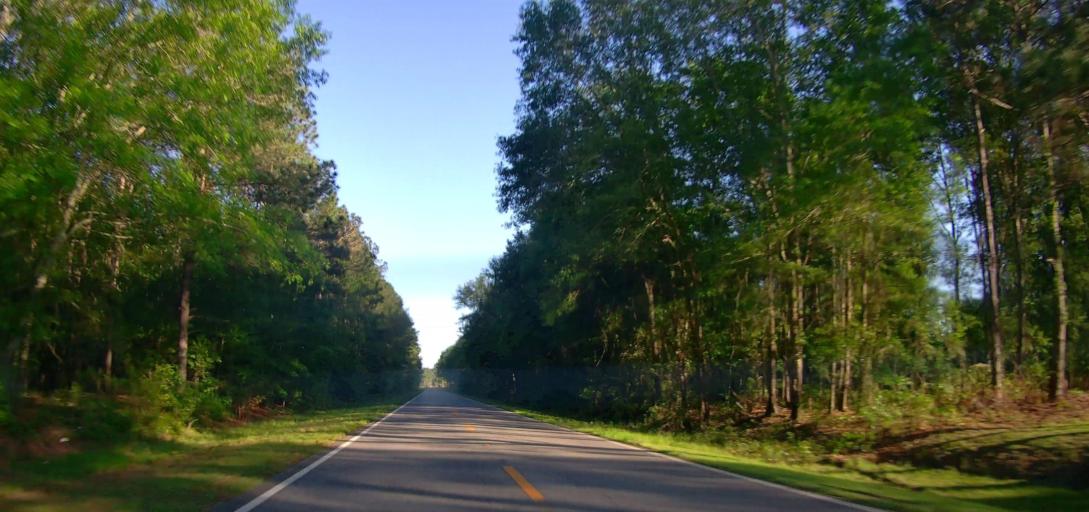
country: US
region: Georgia
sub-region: Ben Hill County
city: Fitzgerald
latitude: 31.6903
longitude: -83.2159
